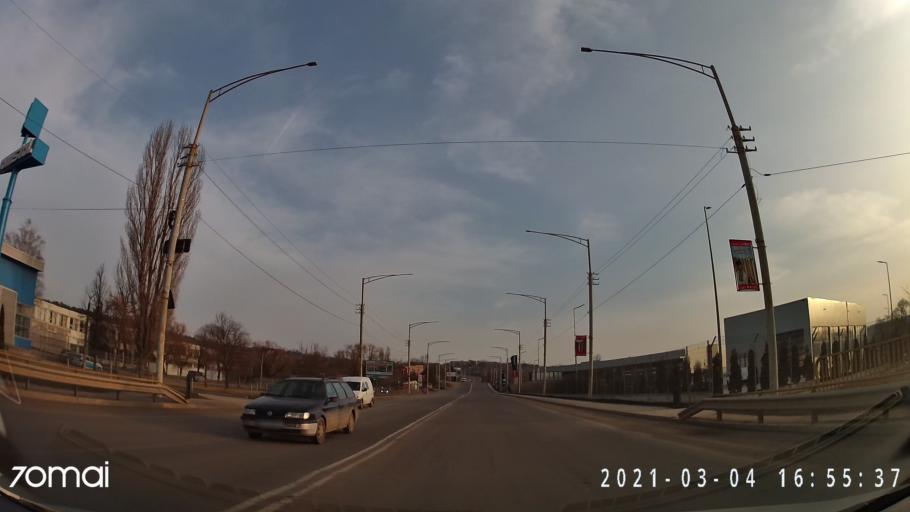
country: MD
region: Balti
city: Balti
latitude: 47.7550
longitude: 27.9418
